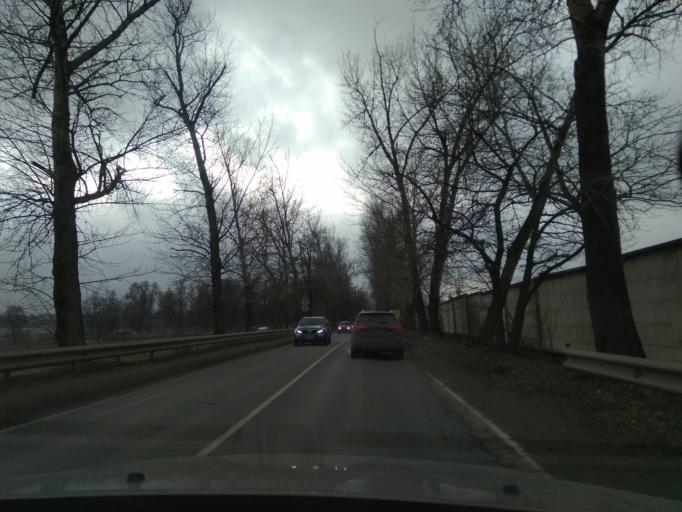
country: RU
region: Moscow
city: Zagor'ye
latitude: 55.5648
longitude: 37.6872
